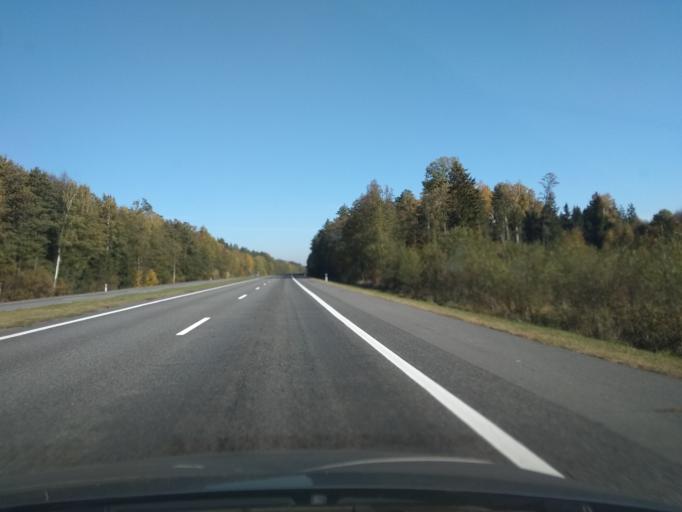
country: BY
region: Brest
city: Nyakhachava
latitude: 52.6473
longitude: 25.2445
